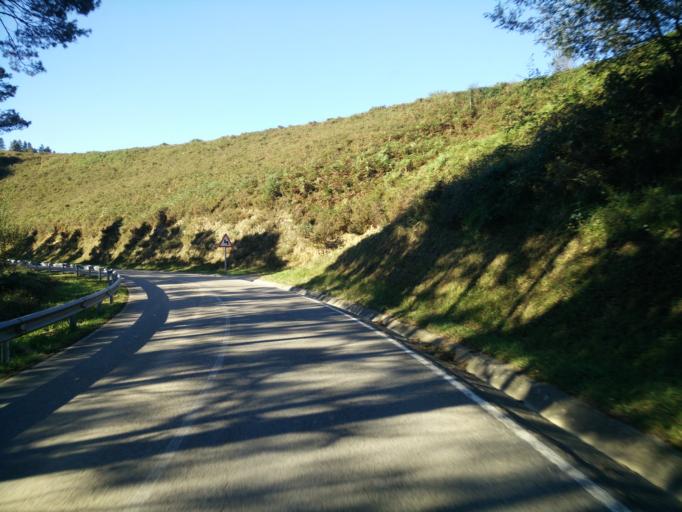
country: ES
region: Cantabria
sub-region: Provincia de Cantabria
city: Vega de Pas
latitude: 43.1820
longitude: -3.8015
